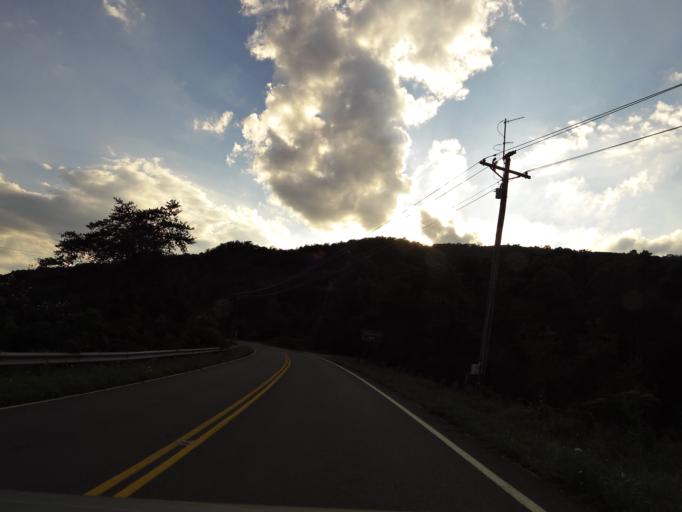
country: US
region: Tennessee
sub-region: Loudon County
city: Greenback
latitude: 35.5574
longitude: -84.0090
